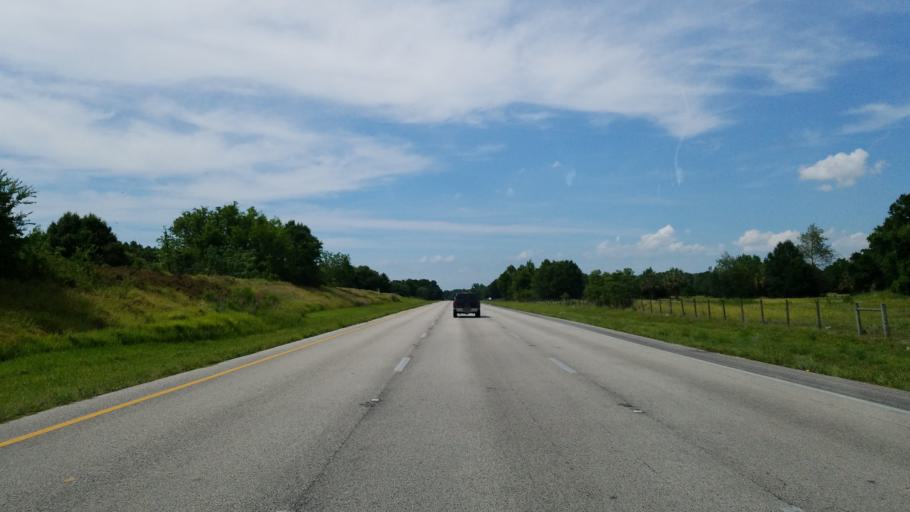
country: US
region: Florida
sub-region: Hardee County
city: Zolfo Springs
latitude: 27.5157
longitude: -81.8043
